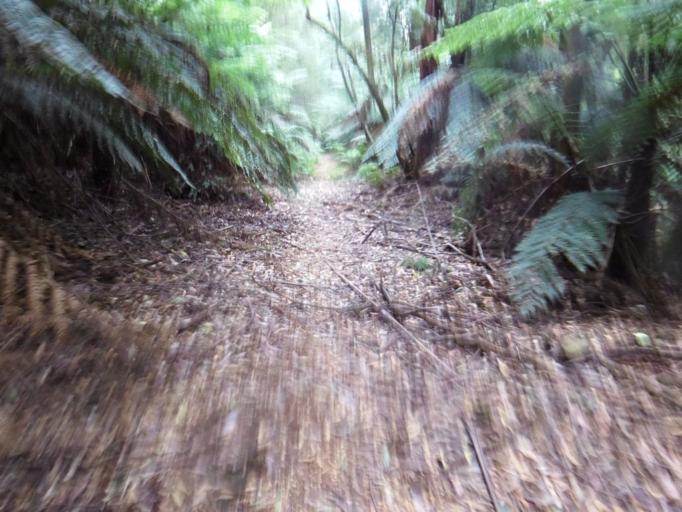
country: AU
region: Victoria
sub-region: Yarra Ranges
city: Healesville
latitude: -37.5172
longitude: 145.5206
